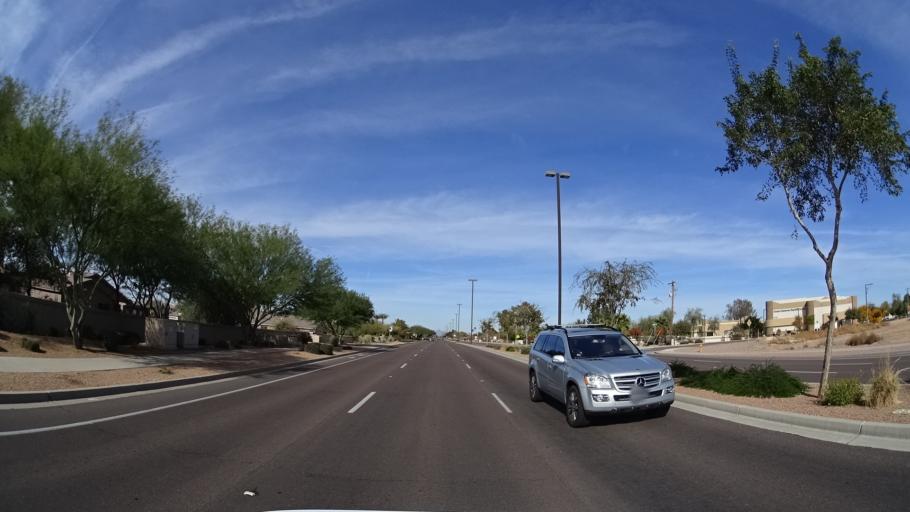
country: US
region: Arizona
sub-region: Maricopa County
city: Gilbert
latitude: 33.3098
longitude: -111.7899
